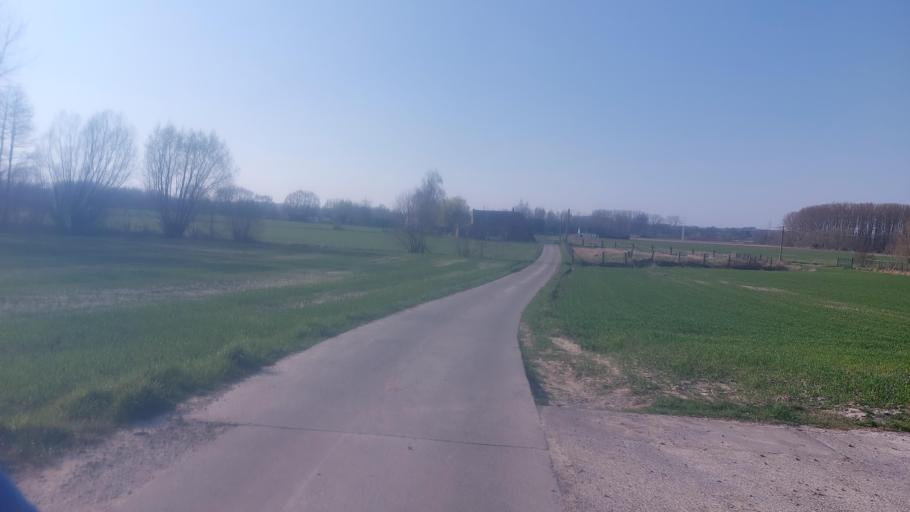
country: BE
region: Wallonia
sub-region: Province du Hainaut
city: Lessines
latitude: 50.6783
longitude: 3.8392
